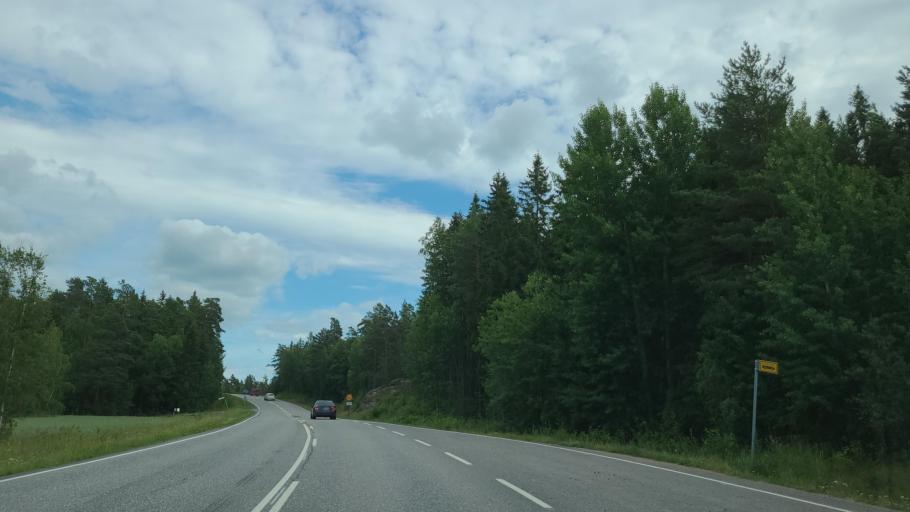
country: FI
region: Varsinais-Suomi
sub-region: Turku
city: Rymaettylae
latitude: 60.3914
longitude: 21.9075
